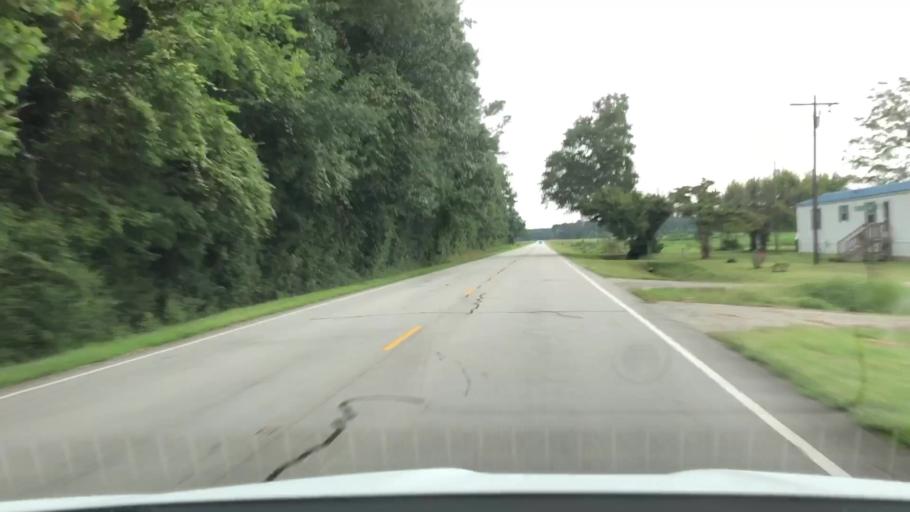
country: US
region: North Carolina
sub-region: Jones County
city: Trenton
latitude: 35.1028
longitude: -77.4932
